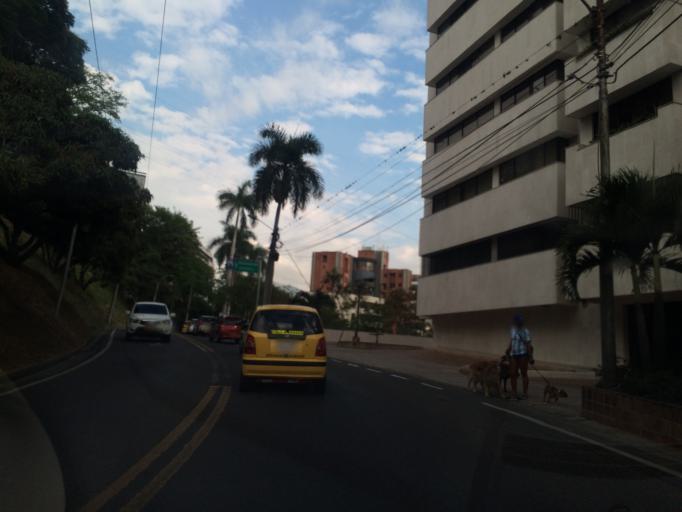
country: CO
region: Valle del Cauca
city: Cali
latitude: 3.4494
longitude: -76.5448
